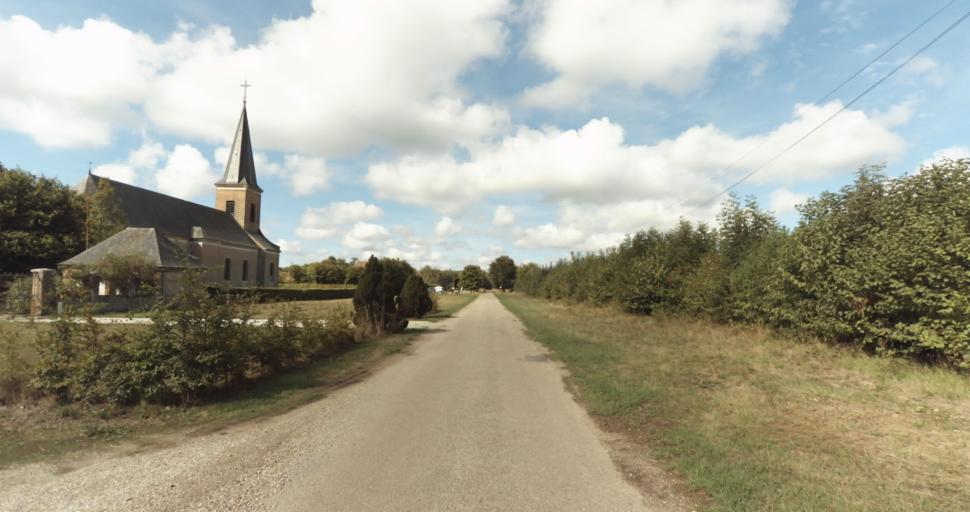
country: FR
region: Lower Normandy
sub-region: Departement du Calvados
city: La Vespiere
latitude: 48.9398
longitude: 0.3213
